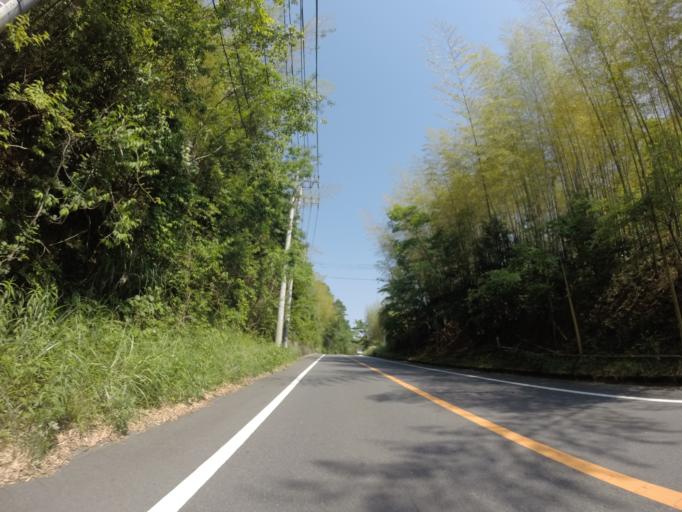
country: JP
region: Shizuoka
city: Fujinomiya
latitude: 35.1994
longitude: 138.5777
